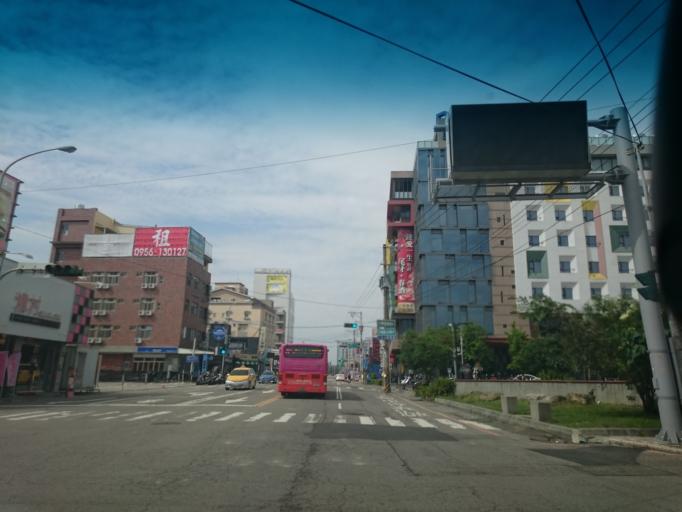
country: TW
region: Taiwan
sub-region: Taichung City
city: Taichung
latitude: 24.1824
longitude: 120.6450
